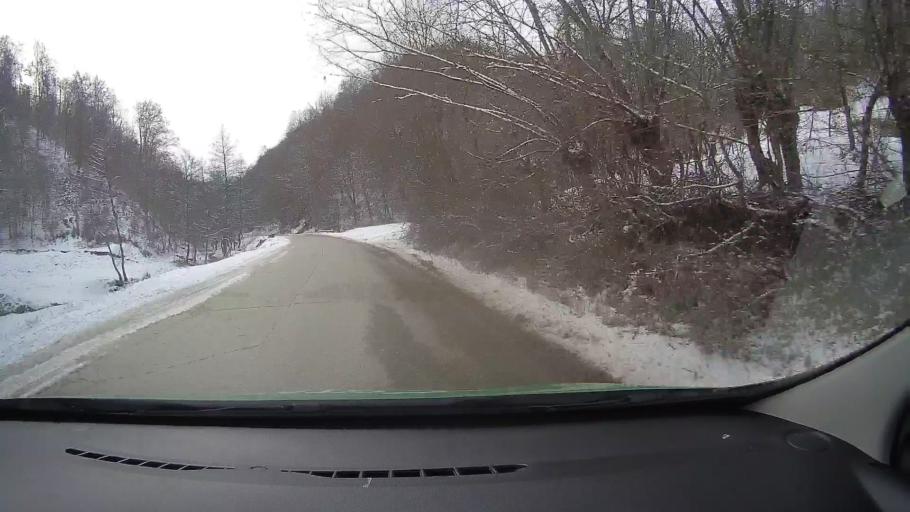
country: RO
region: Alba
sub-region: Oras Zlatna
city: Zlatna
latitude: 46.1068
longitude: 23.1948
